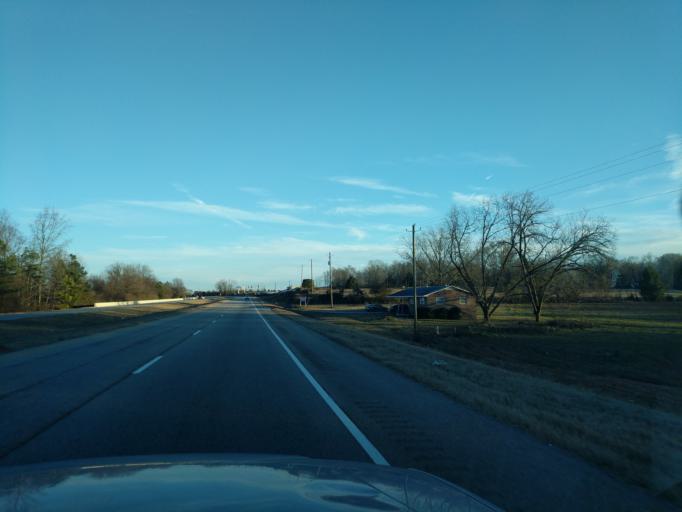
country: US
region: Georgia
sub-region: Franklin County
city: Lavonia
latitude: 34.4513
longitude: -83.1479
